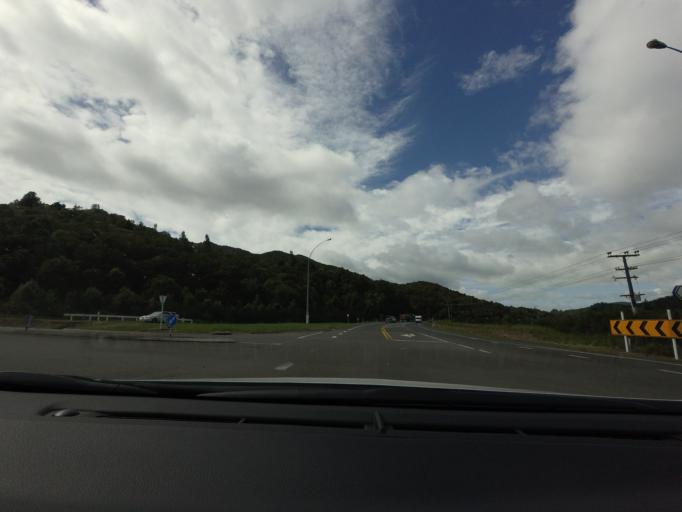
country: NZ
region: Bay of Plenty
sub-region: Rotorua District
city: Rotorua
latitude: -38.3110
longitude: 176.3776
